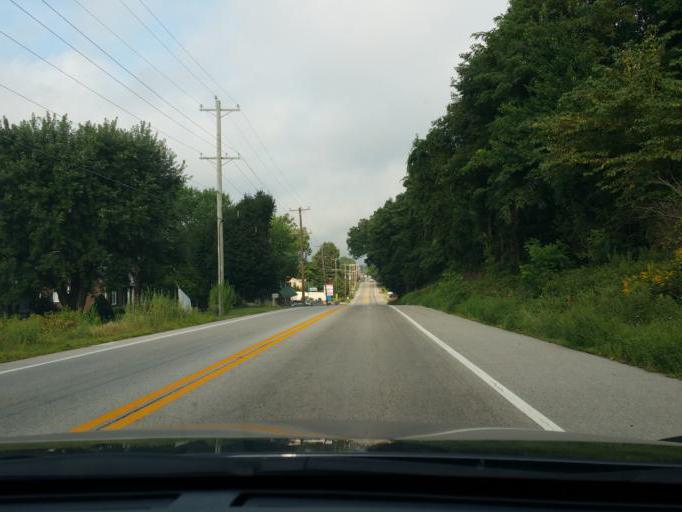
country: US
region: Maryland
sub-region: Cecil County
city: Rising Sun
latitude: 39.6940
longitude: -76.1038
